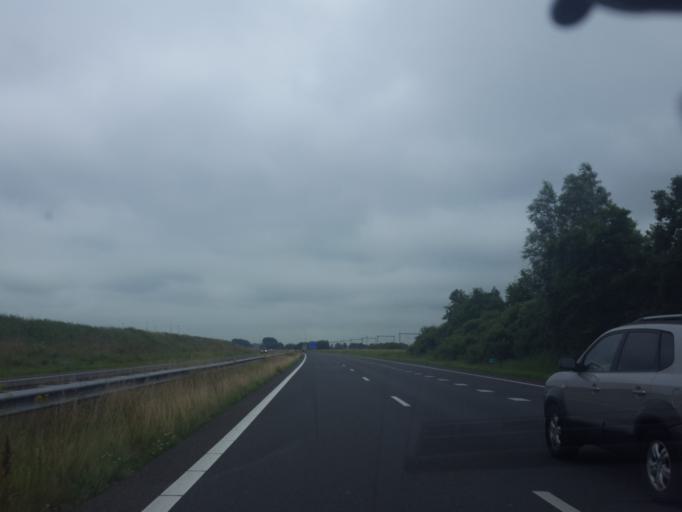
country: NL
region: Friesland
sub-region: Gemeente Boarnsterhim
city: Grou
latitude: 53.1057
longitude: 5.8156
